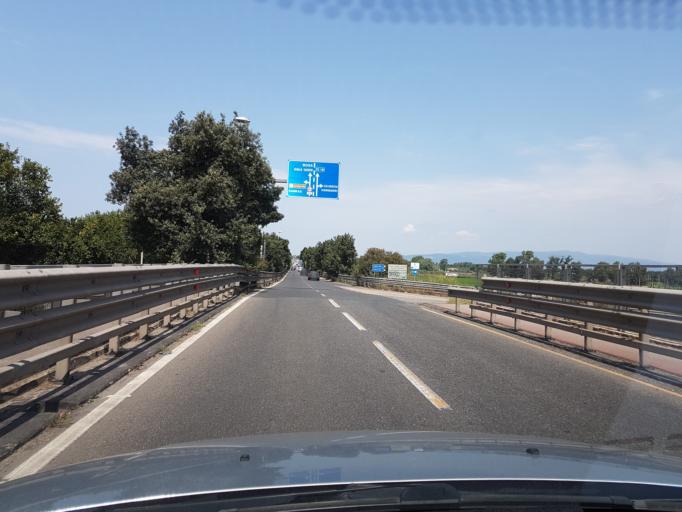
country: IT
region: Sardinia
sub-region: Provincia di Oristano
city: Donigala Fenugheddu
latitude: 39.9222
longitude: 8.5815
